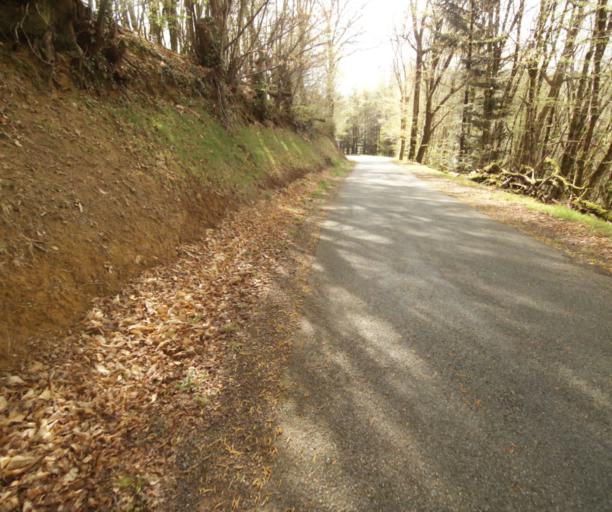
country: FR
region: Limousin
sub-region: Departement de la Correze
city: Laguenne
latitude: 45.2599
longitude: 1.8260
